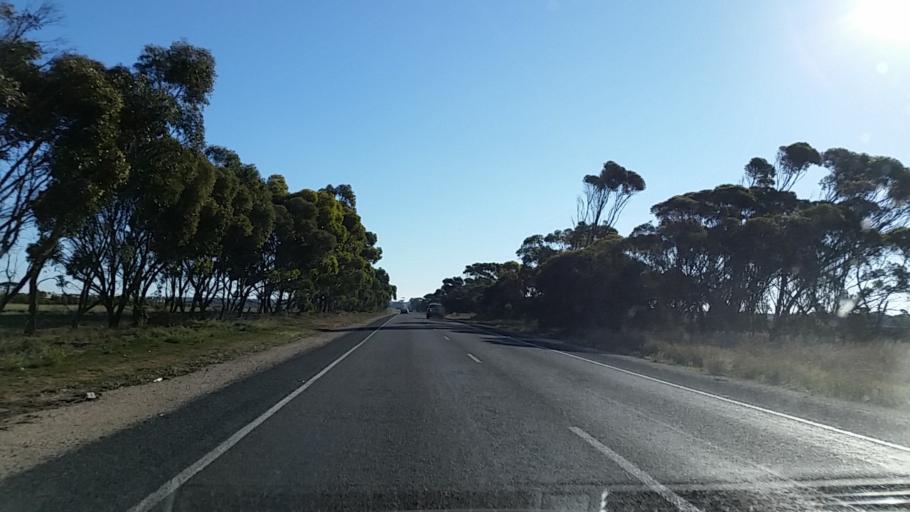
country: AU
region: South Australia
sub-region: Mount Barker
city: Callington
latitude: -35.1173
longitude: 139.1230
